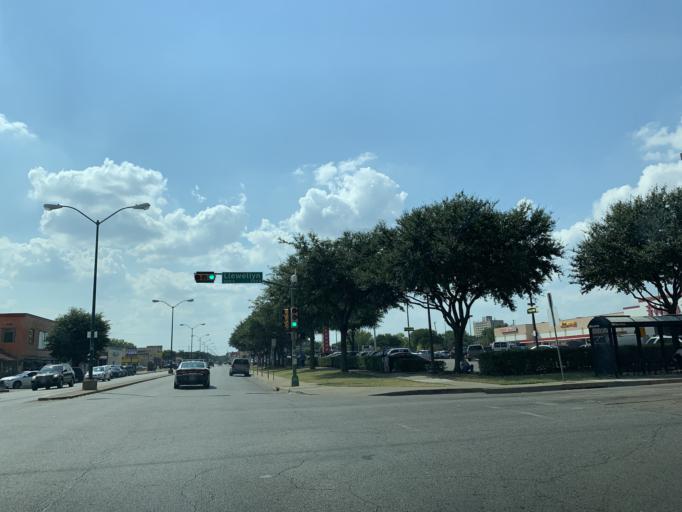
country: US
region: Texas
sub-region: Dallas County
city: Dallas
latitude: 32.7432
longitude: -96.8320
